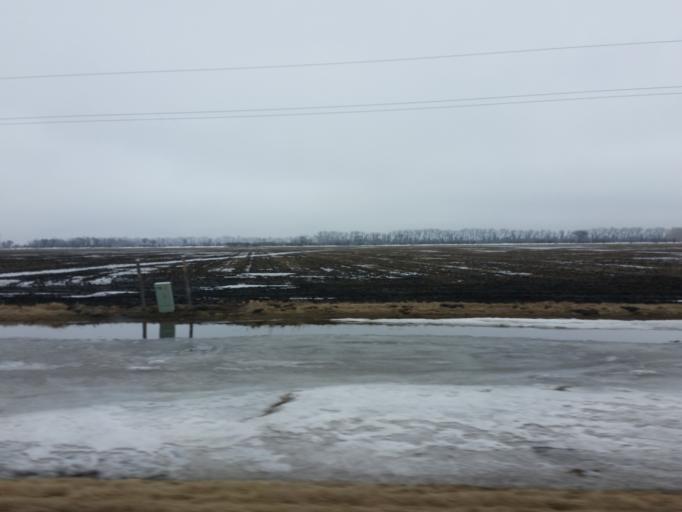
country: US
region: North Dakota
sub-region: Walsh County
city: Grafton
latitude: 48.5720
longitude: -97.4336
